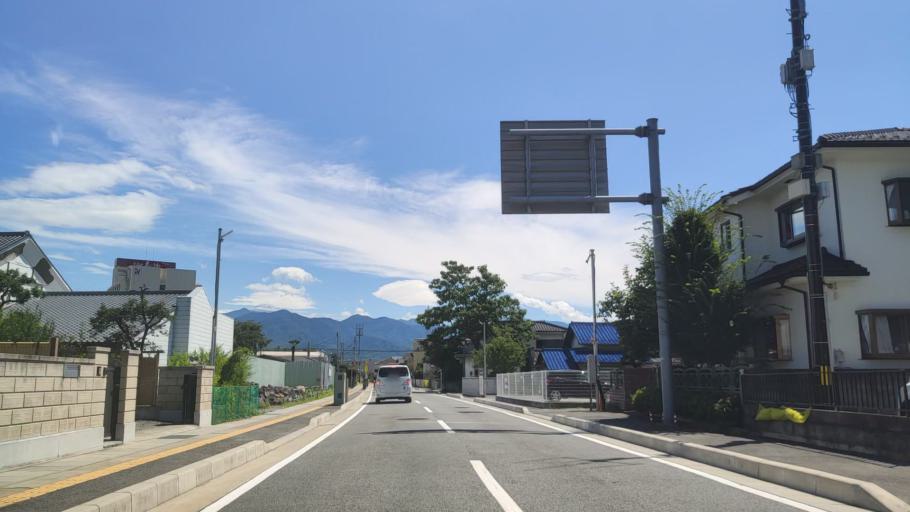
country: JP
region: Yamanashi
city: Isawa
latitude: 35.6593
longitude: 138.6382
